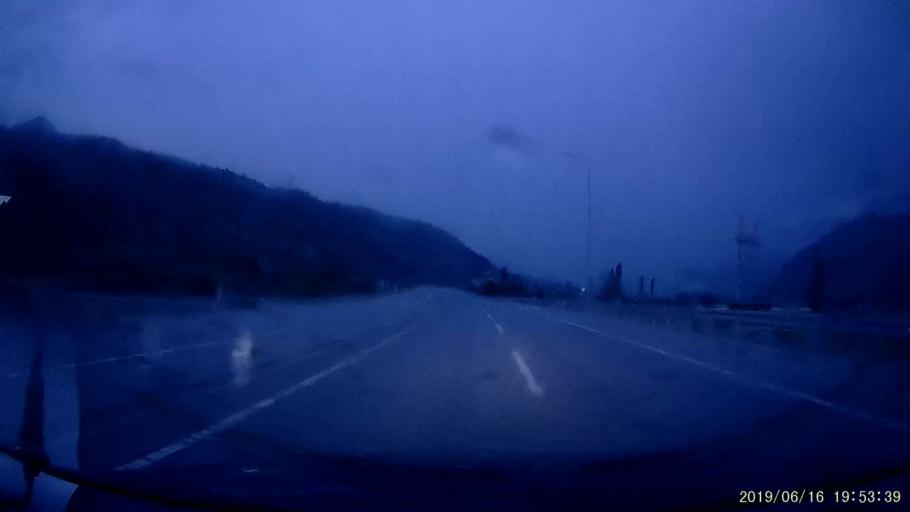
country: TR
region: Sivas
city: Koyulhisar
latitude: 40.2888
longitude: 37.7806
